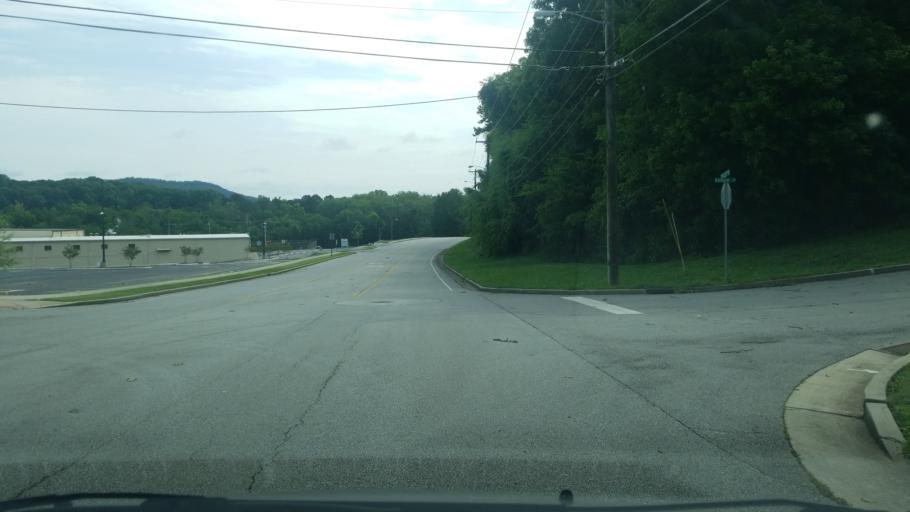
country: US
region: Tennessee
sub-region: Hamilton County
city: Collegedale
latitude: 35.0469
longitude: -85.0409
